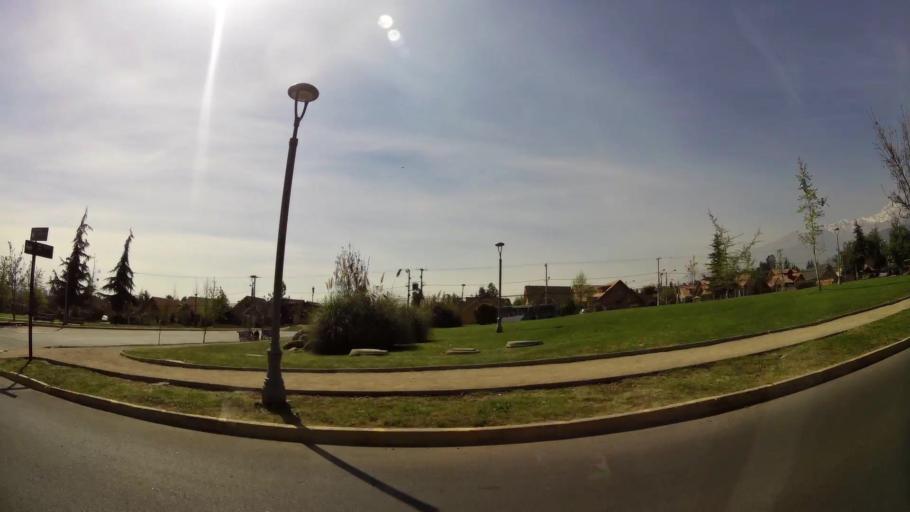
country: CL
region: Santiago Metropolitan
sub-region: Provincia de Cordillera
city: Puente Alto
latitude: -33.5359
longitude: -70.5493
